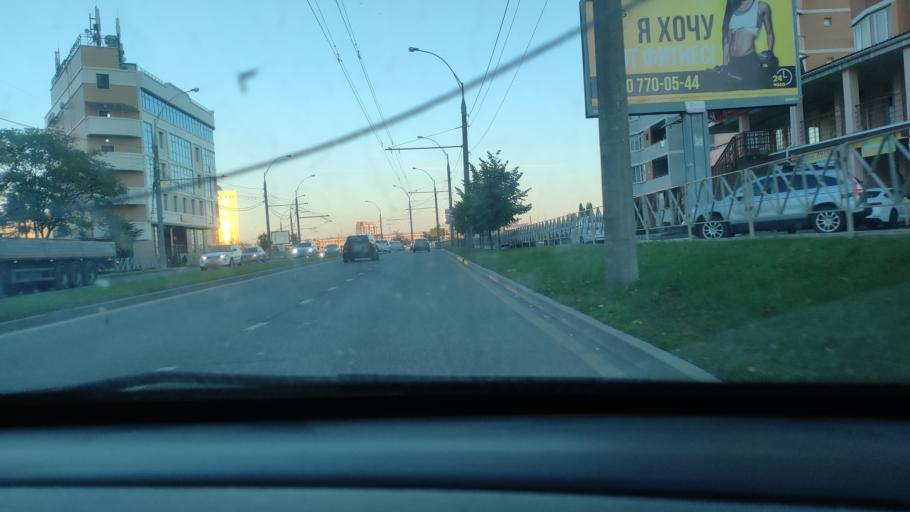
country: RU
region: Krasnodarskiy
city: Krasnodar
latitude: 45.0384
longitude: 38.9491
